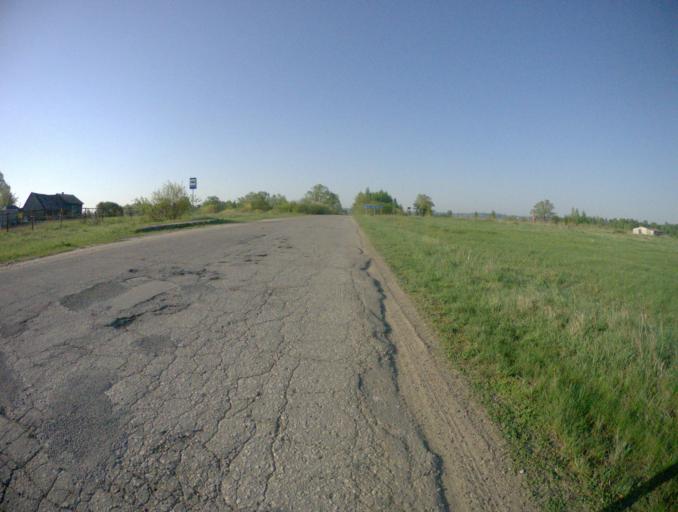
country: RU
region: Vladimir
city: Vyazniki
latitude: 56.2711
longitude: 42.1719
